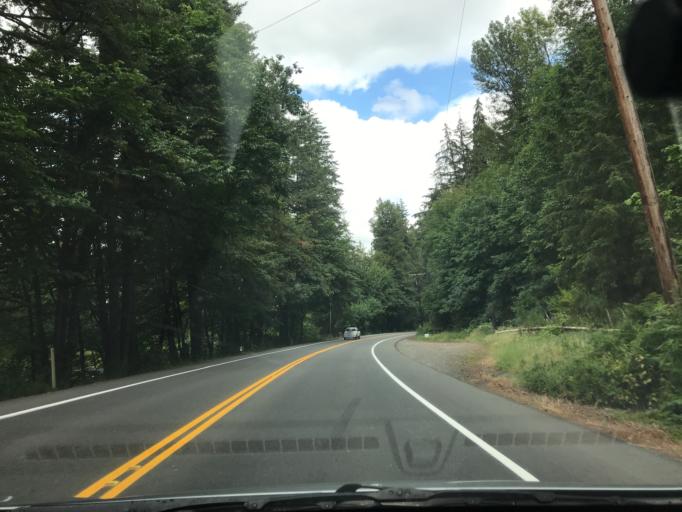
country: US
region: Washington
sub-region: King County
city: Lea Hill
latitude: 47.3164
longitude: -122.1506
